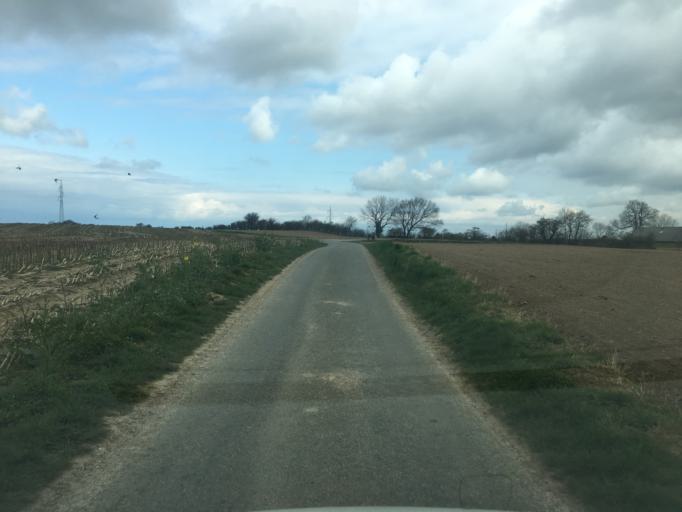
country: DK
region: South Denmark
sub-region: Sonderborg Kommune
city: Grasten
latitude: 54.9927
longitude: 9.5261
